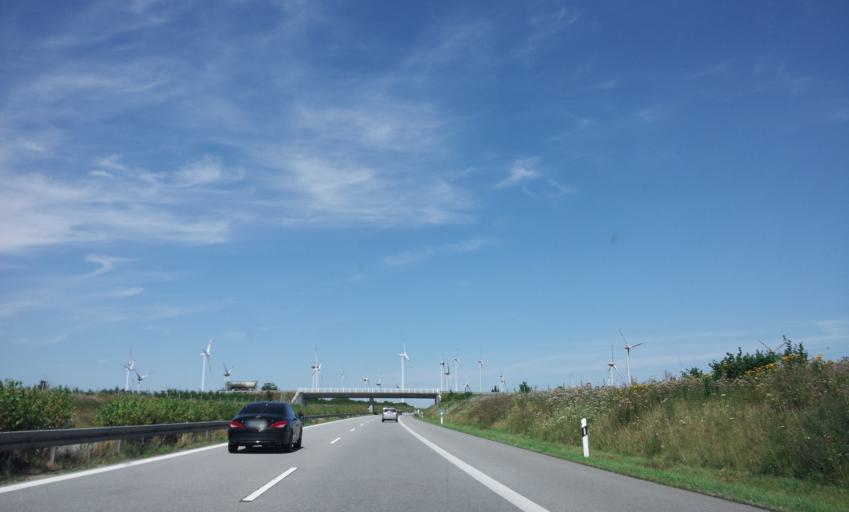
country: DE
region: Mecklenburg-Vorpommern
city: Kessin
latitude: 53.6940
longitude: 13.3258
